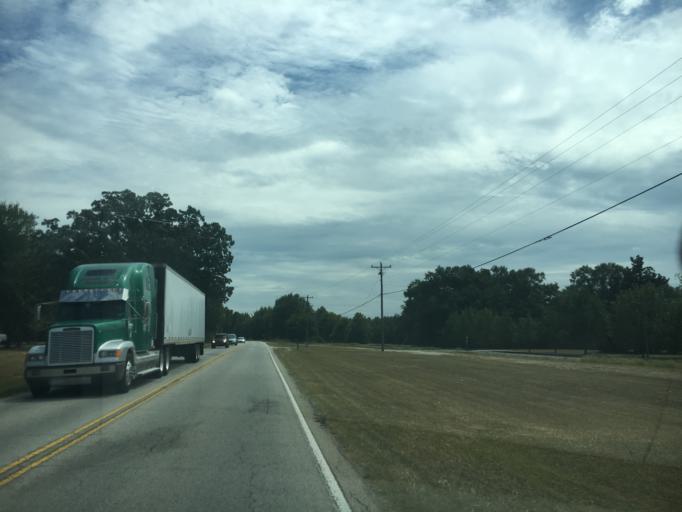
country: US
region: South Carolina
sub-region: Laurens County
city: Laurens
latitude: 34.5424
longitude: -82.0676
